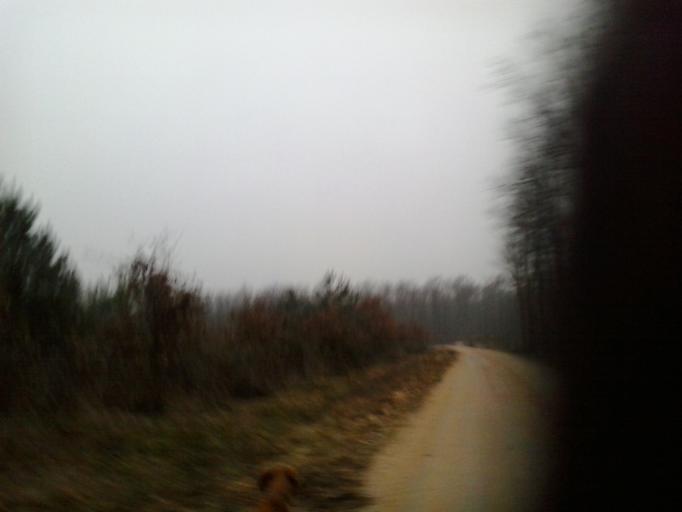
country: HU
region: Vas
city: Sarvar
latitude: 47.1378
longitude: 16.9768
